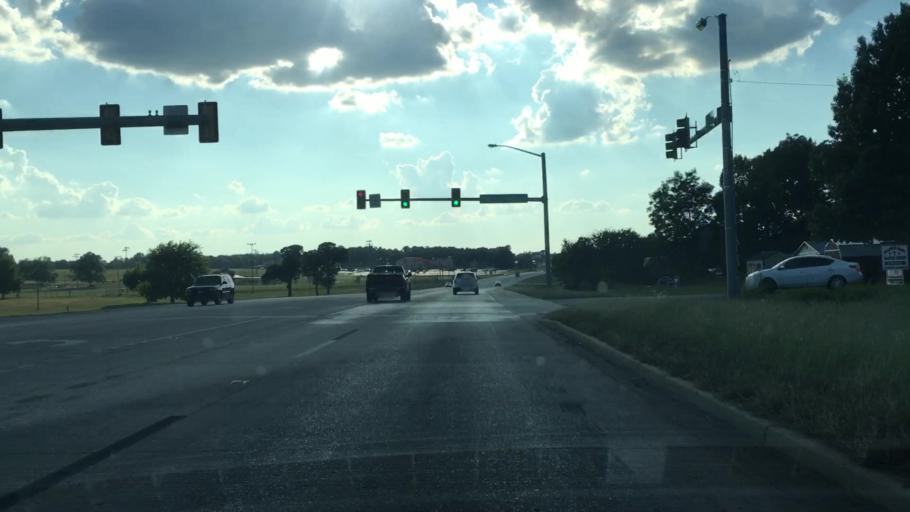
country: US
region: Oklahoma
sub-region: Cherokee County
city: Park Hill
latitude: 35.8490
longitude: -95.0022
